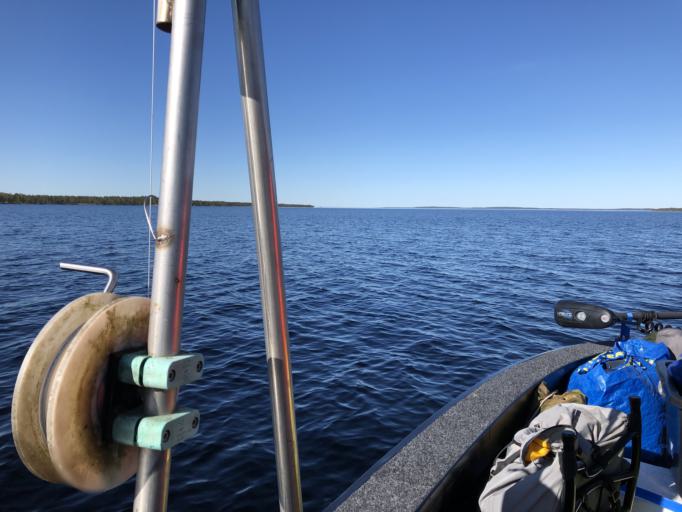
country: FI
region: Lapland
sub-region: Pohjois-Lappi
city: Ivalo
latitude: 68.9552
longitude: 27.8881
